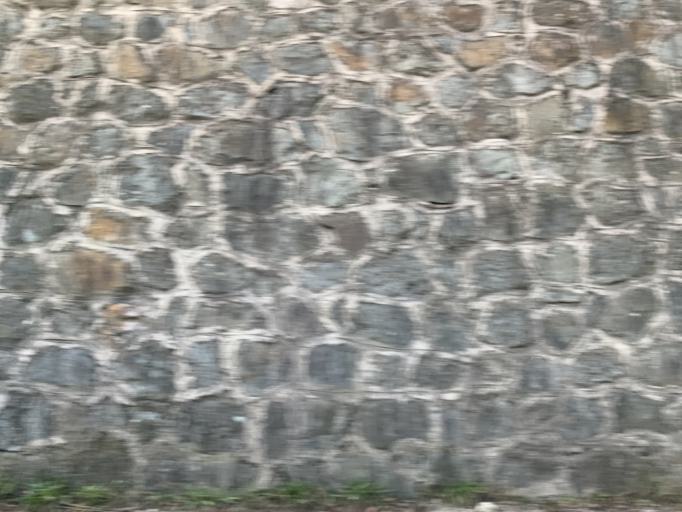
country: TR
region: Trabzon
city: Dernekpazari
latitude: 40.8423
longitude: 40.2811
